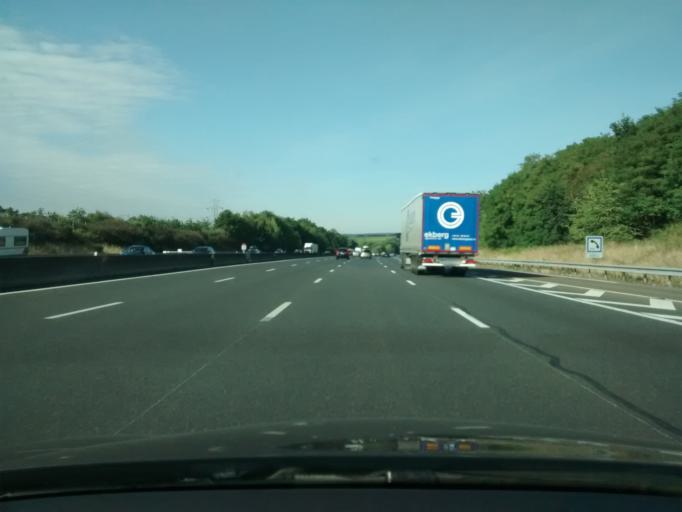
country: FR
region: Ile-de-France
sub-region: Departement de l'Essonne
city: Briis-sous-Forges
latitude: 48.6170
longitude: 2.1262
